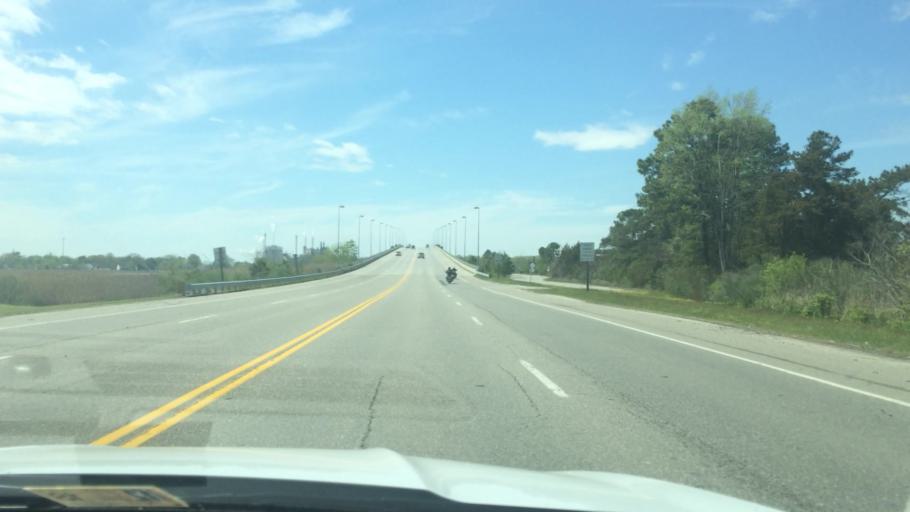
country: US
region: Virginia
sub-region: King William County
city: West Point
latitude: 37.5350
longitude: -76.7810
